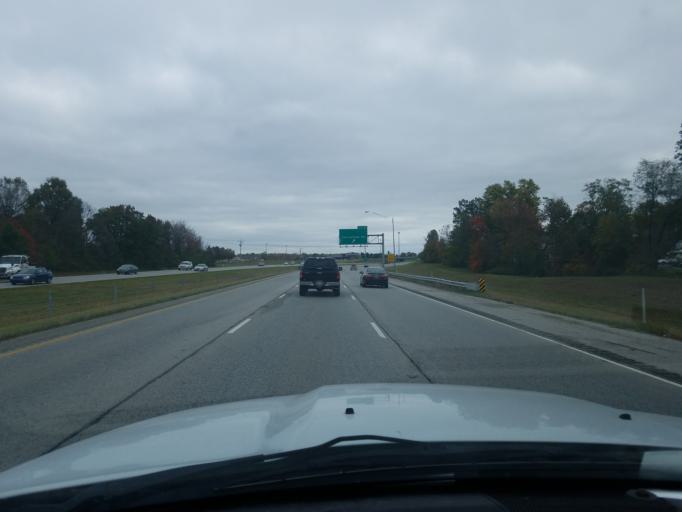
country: US
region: Indiana
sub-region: Floyd County
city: New Albany
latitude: 38.3418
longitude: -85.8057
